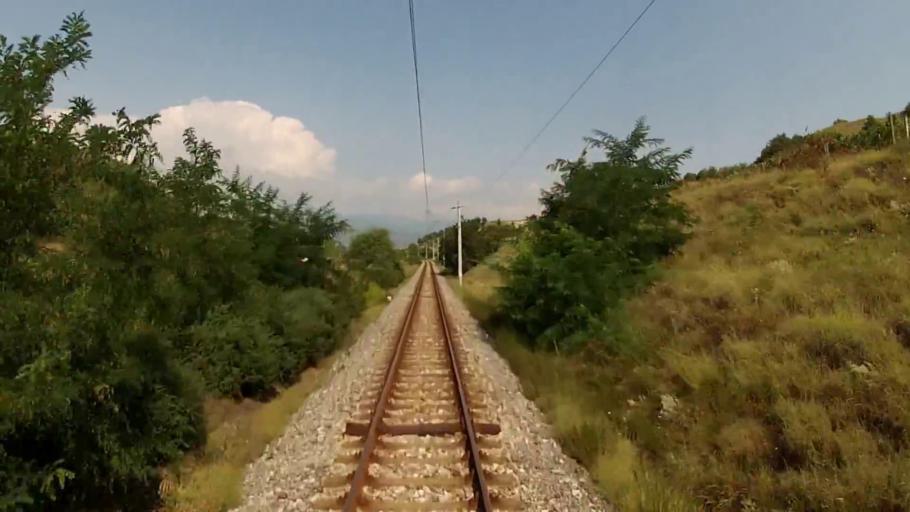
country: BG
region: Blagoevgrad
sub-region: Obshtina Strumyani
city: Strumyani
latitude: 41.6235
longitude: 23.2158
